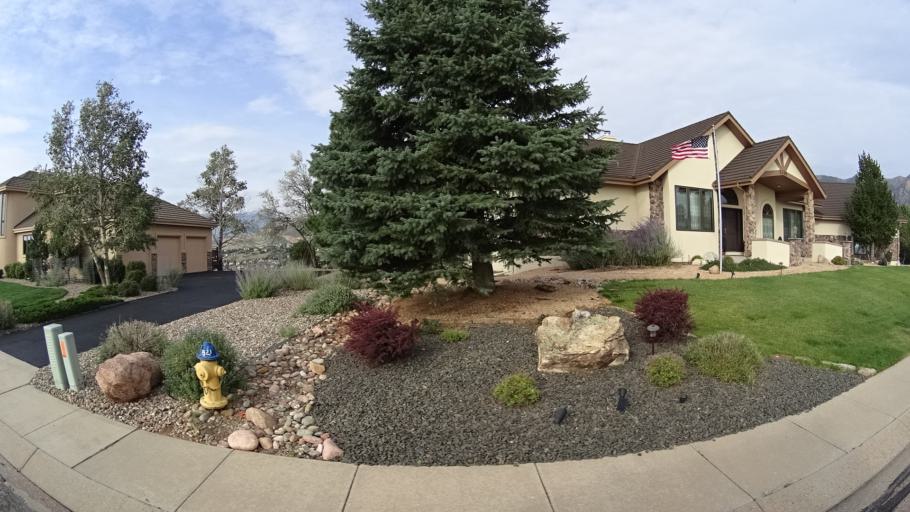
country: US
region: Colorado
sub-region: El Paso County
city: Air Force Academy
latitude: 38.9330
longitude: -104.8609
